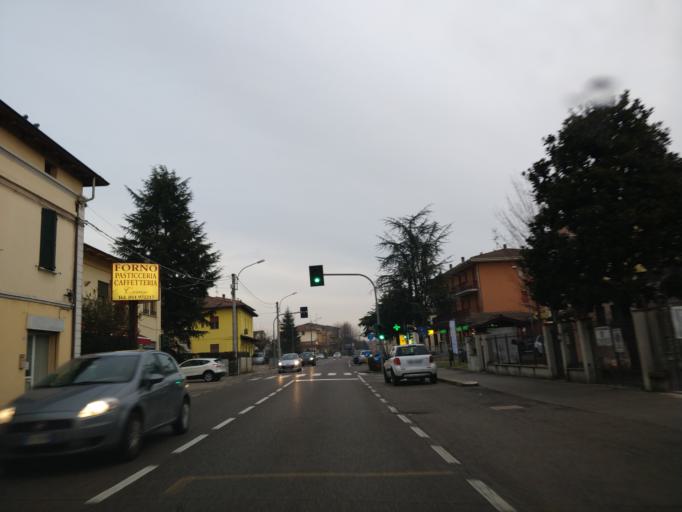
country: IT
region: Emilia-Romagna
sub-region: Provincia di Ferrara
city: Corpo Reno
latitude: 44.7585
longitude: 11.3131
